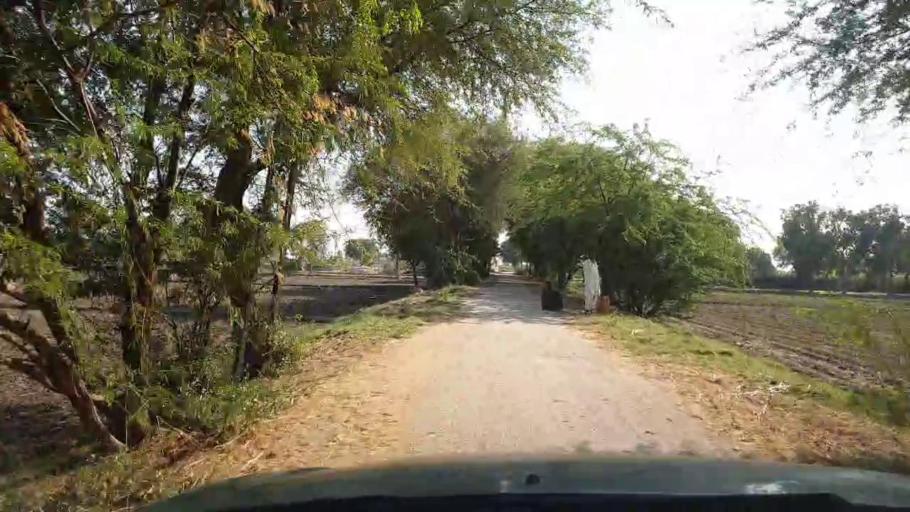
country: PK
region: Sindh
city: Tando Muhammad Khan
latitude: 25.1015
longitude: 68.5825
